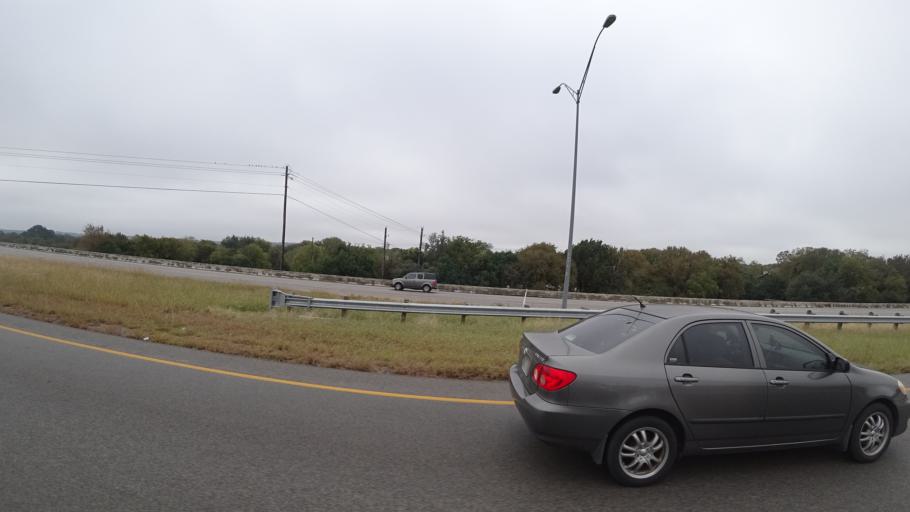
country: US
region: Texas
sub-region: Travis County
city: Shady Hollow
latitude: 30.2168
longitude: -97.8487
